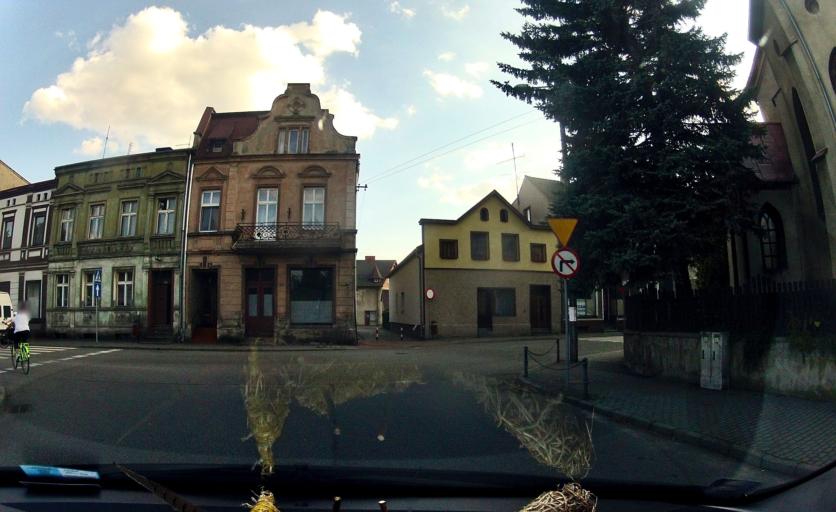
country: PL
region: Opole Voivodeship
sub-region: Powiat oleski
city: Gorzow Slaski
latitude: 51.0281
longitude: 18.4219
